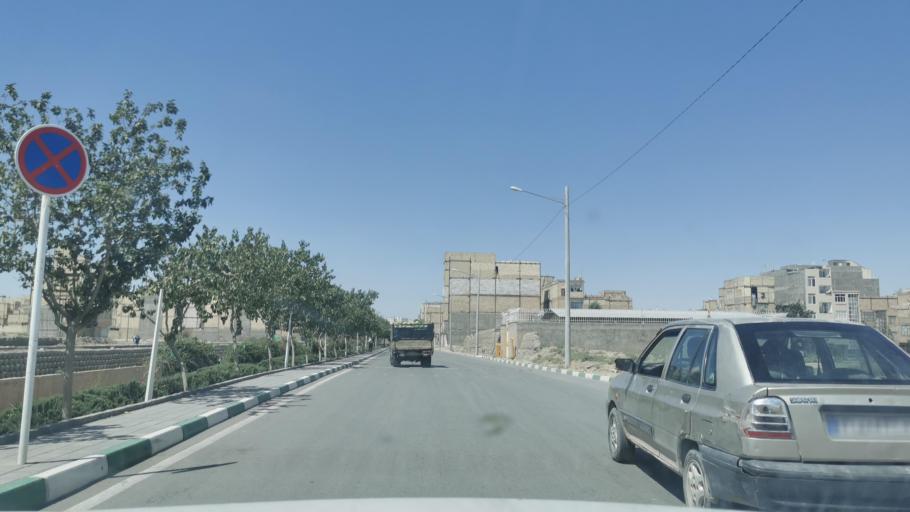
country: IR
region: Razavi Khorasan
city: Mashhad
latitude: 36.3578
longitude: 59.5640
